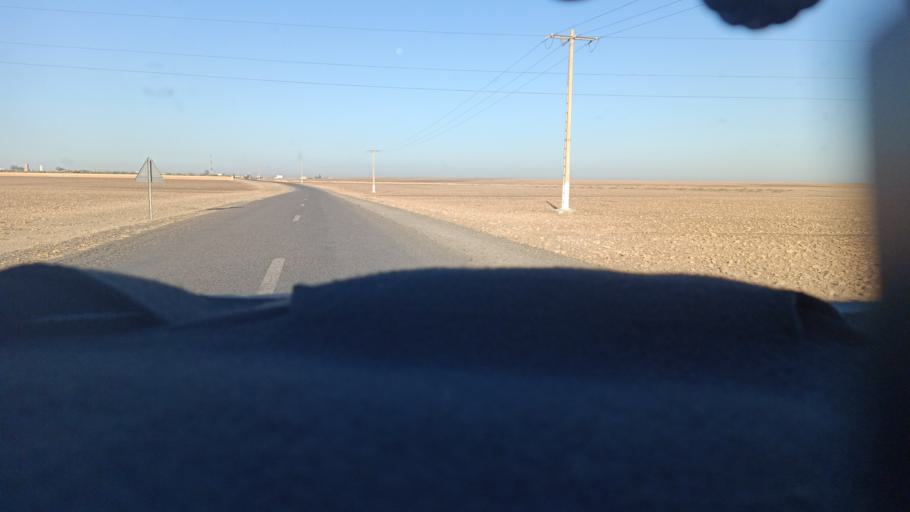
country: MA
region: Doukkala-Abda
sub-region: Safi
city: Youssoufia
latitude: 32.3711
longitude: -8.6628
